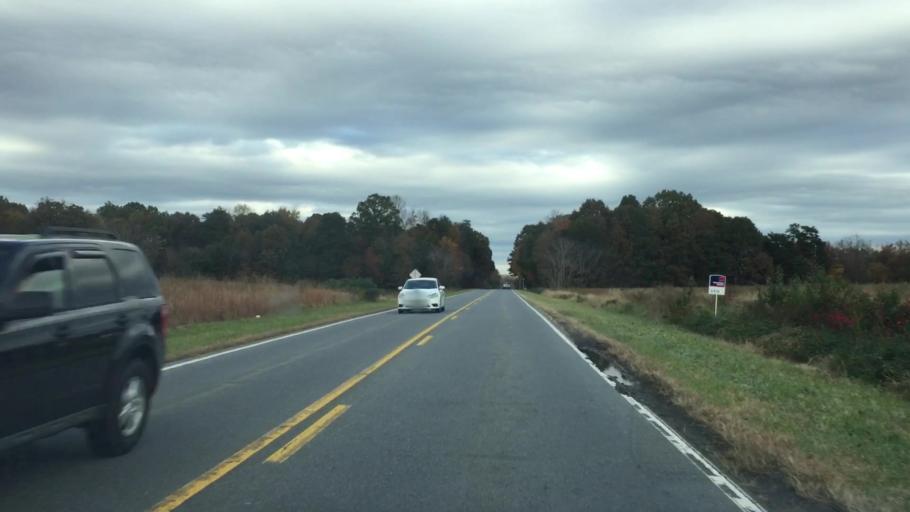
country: US
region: North Carolina
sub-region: Rockingham County
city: Reidsville
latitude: 36.2925
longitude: -79.7292
